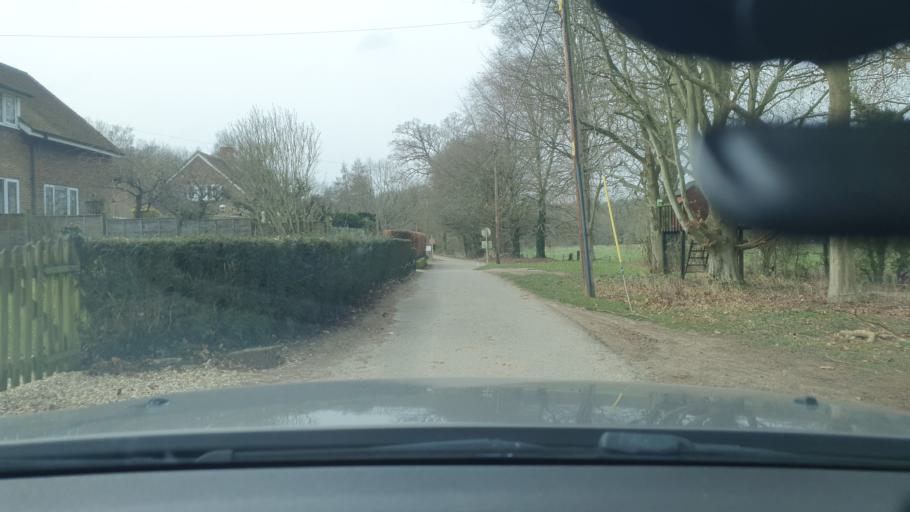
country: GB
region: England
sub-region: Wiltshire
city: Ramsbury
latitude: 51.4365
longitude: -1.6231
